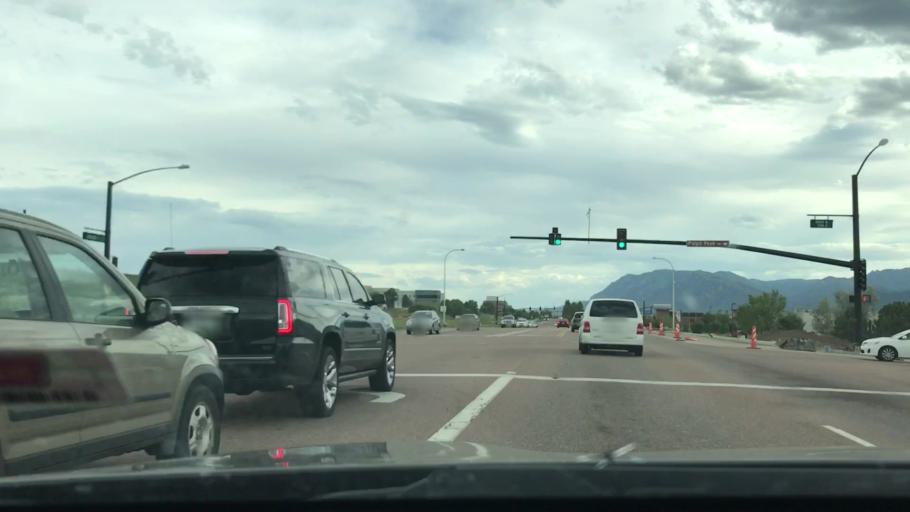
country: US
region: Colorado
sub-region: El Paso County
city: Colorado Springs
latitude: 38.9105
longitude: -104.8162
